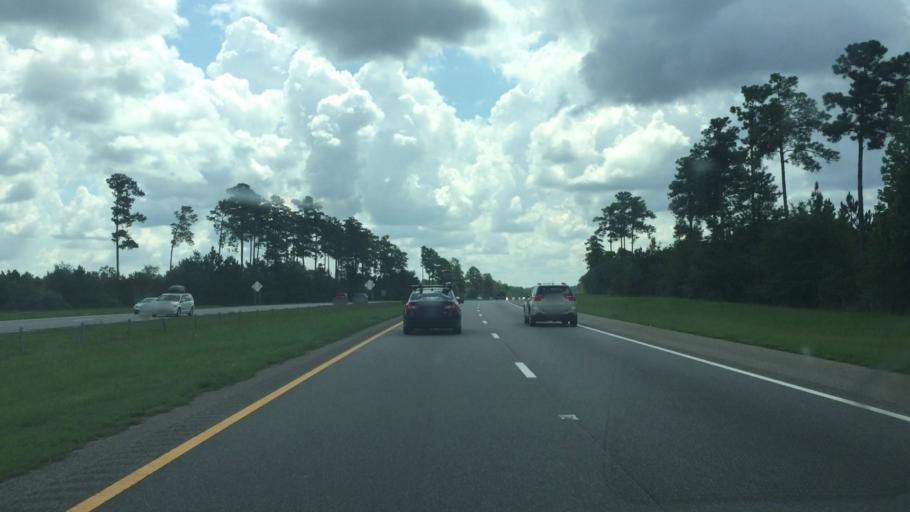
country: US
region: North Carolina
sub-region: Richmond County
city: East Rockingham
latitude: 34.8685
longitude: -79.7554
